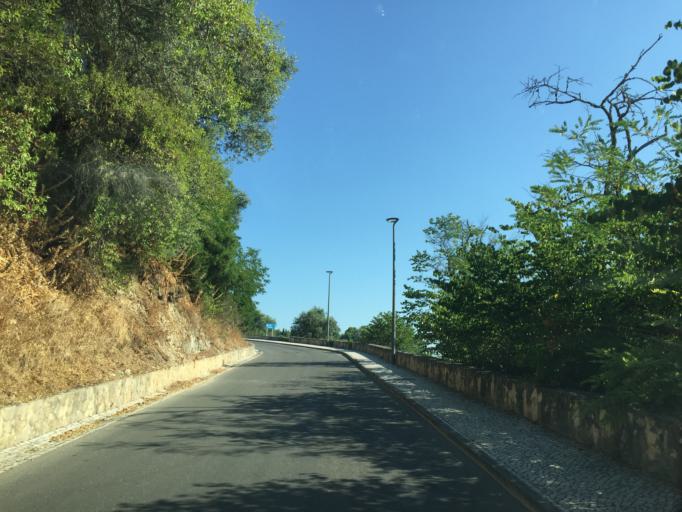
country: PT
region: Santarem
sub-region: Tomar
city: Tomar
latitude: 39.6042
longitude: -8.4160
